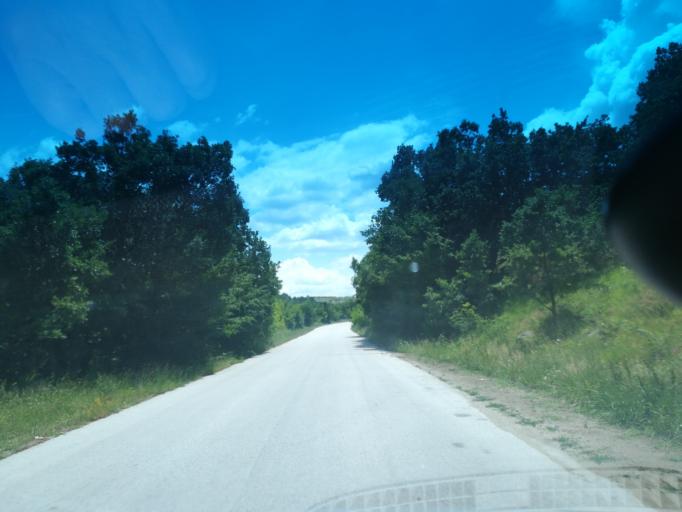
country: BG
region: Khaskovo
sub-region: Obshtina Mineralni Bani
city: Mineralni Bani
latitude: 41.9709
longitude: 25.2605
